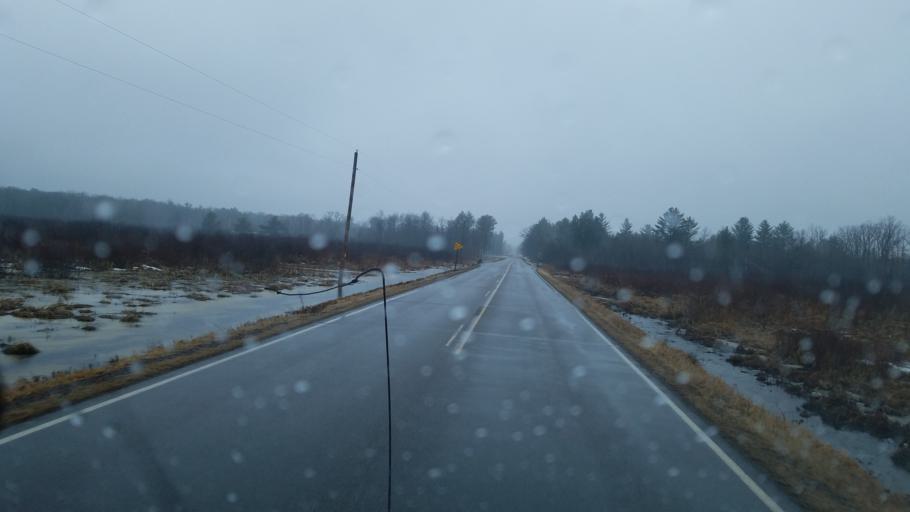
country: US
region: Wisconsin
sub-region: Wood County
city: Marshfield
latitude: 44.5080
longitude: -90.2792
